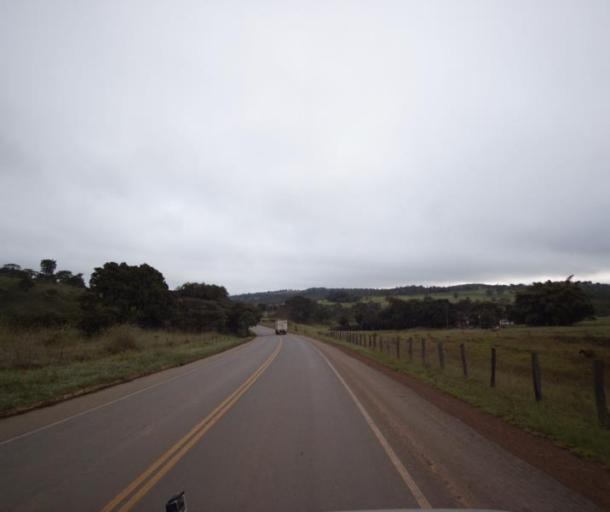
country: BR
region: Goias
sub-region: Pirenopolis
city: Pirenopolis
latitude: -15.9507
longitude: -48.8040
